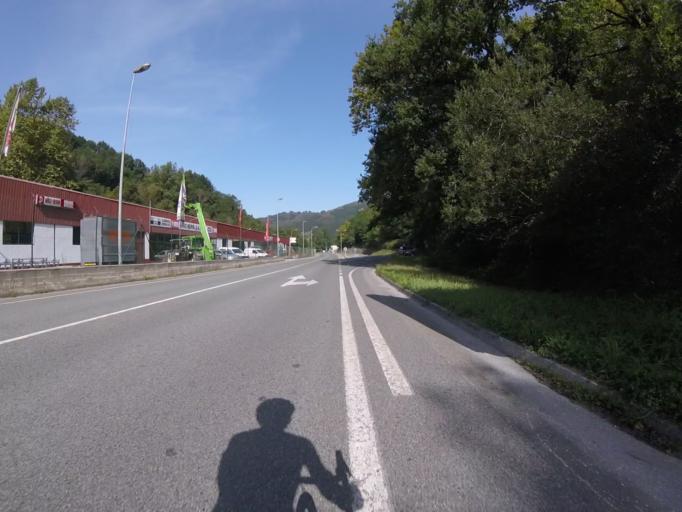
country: ES
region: Navarre
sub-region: Provincia de Navarra
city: Doneztebe
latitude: 43.1355
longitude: -1.5540
